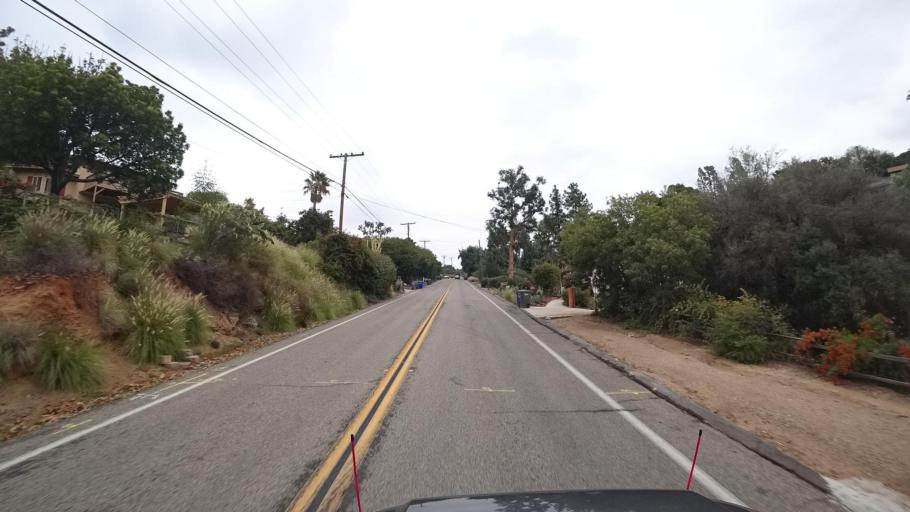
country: US
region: California
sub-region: San Diego County
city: Casa de Oro-Mount Helix
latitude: 32.7601
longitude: -116.9830
